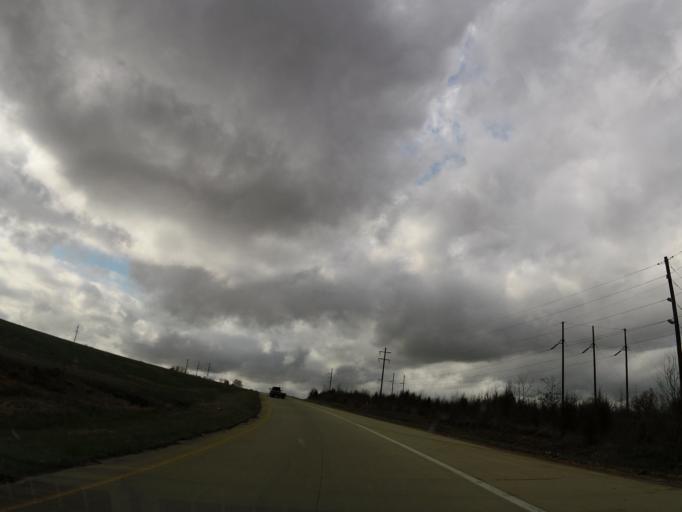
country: US
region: Missouri
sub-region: Butler County
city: Poplar Bluff
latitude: 36.7286
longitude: -90.4637
